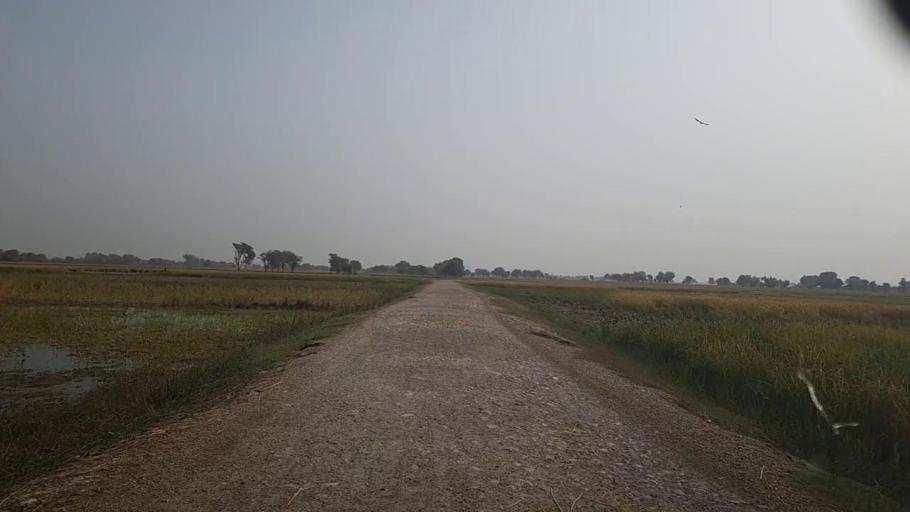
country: PK
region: Sindh
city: Kashmor
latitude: 28.3917
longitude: 69.4245
